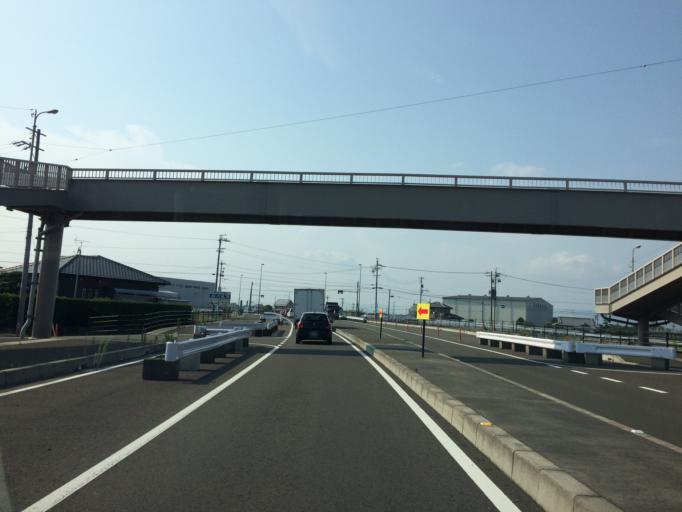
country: JP
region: Shizuoka
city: Yaizu
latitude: 34.8170
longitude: 138.3105
